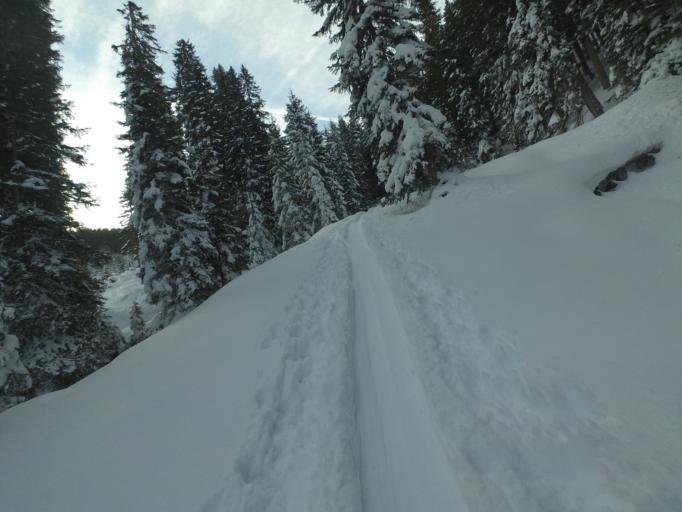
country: AT
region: Salzburg
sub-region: Politischer Bezirk Zell am See
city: Lend
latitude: 47.2751
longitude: 13.0134
